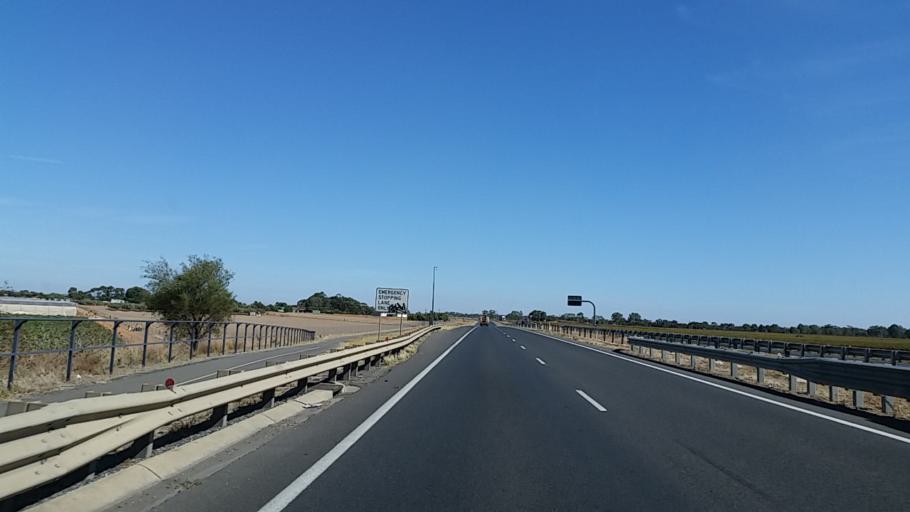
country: AU
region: South Australia
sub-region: Playford
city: Angle Vale
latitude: -34.6159
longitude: 138.6803
